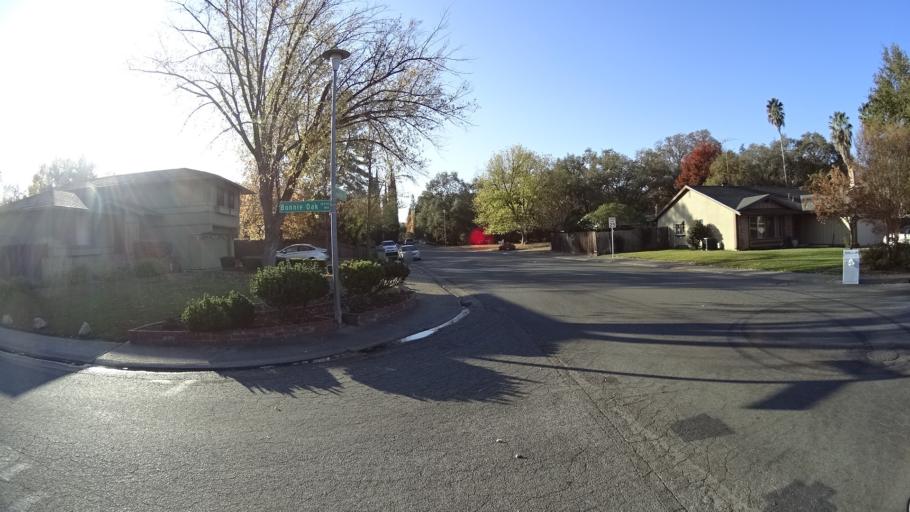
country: US
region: California
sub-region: Sacramento County
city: Citrus Heights
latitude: 38.7189
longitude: -121.2576
